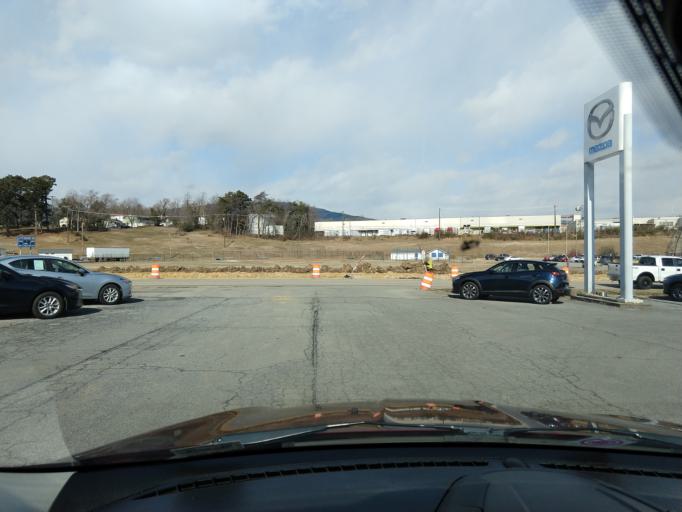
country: US
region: Virginia
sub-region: City of Salem
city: Salem
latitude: 37.2948
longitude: -80.0450
